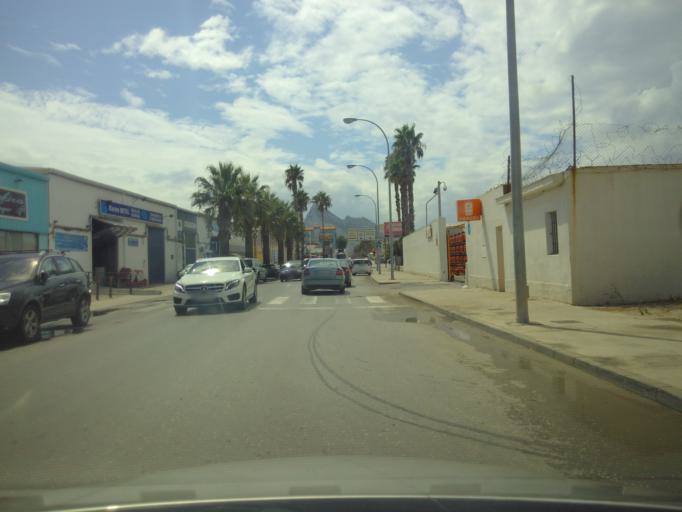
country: ES
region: Andalusia
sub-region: Provincia de Cadiz
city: La Linea de la Concepcion
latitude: 36.1792
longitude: -5.3490
